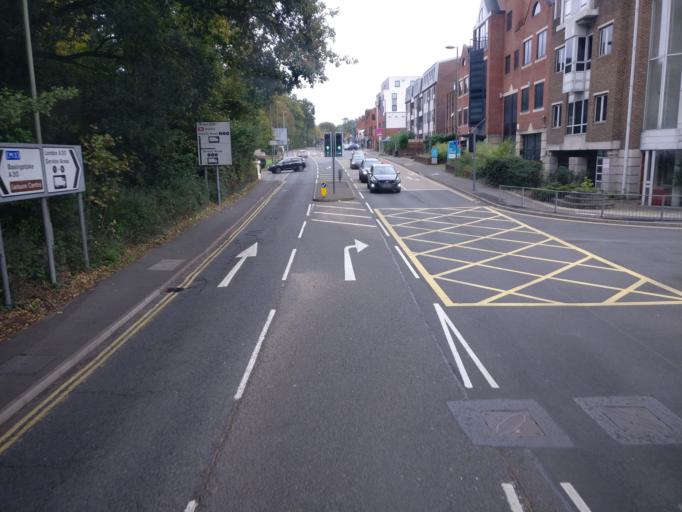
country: GB
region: England
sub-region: Surrey
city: Camberley
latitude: 51.3387
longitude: -0.7507
